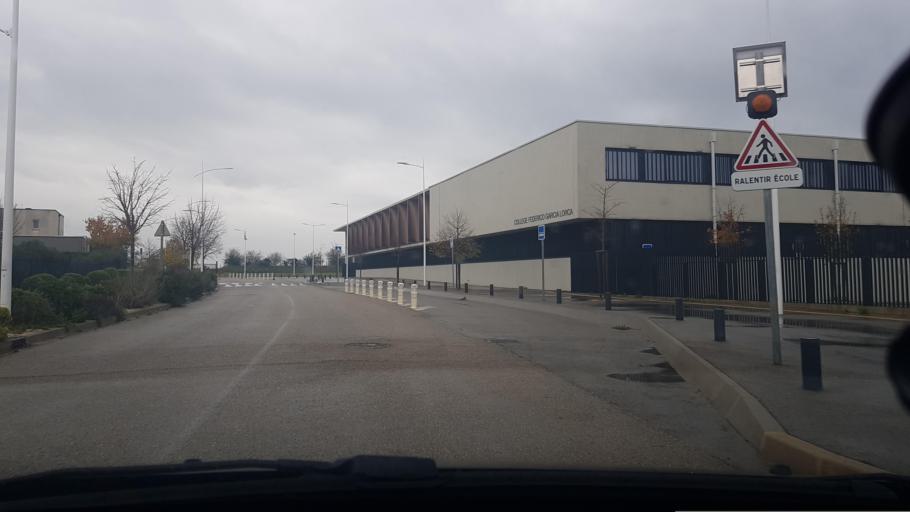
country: FR
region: Languedoc-Roussillon
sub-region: Departement du Gard
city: Bellegarde
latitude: 43.7519
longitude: 4.4957
